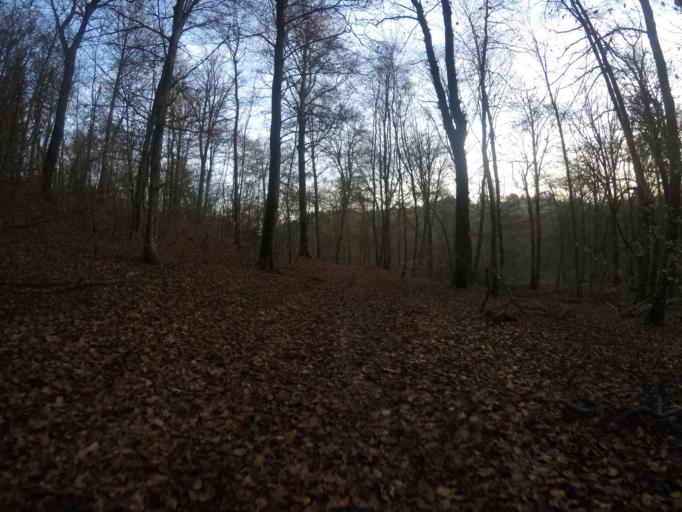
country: BE
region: Wallonia
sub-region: Province du Luxembourg
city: Habay-la-Vieille
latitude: 49.7374
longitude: 5.6682
